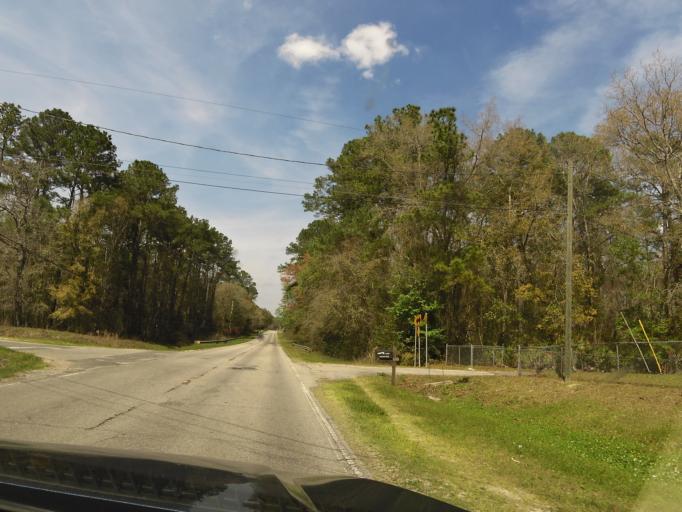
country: US
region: Florida
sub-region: Clay County
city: Middleburg
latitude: 30.1064
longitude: -81.8646
